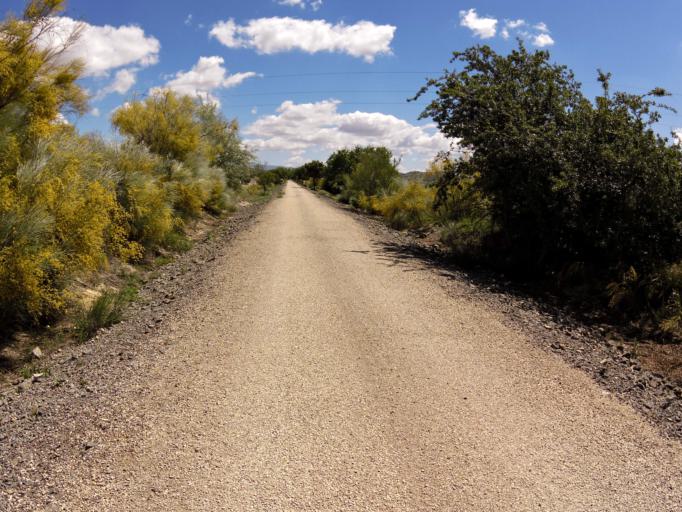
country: ES
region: Andalusia
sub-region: Provincia de Jaen
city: Alcaudete
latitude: 37.6481
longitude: -4.0676
